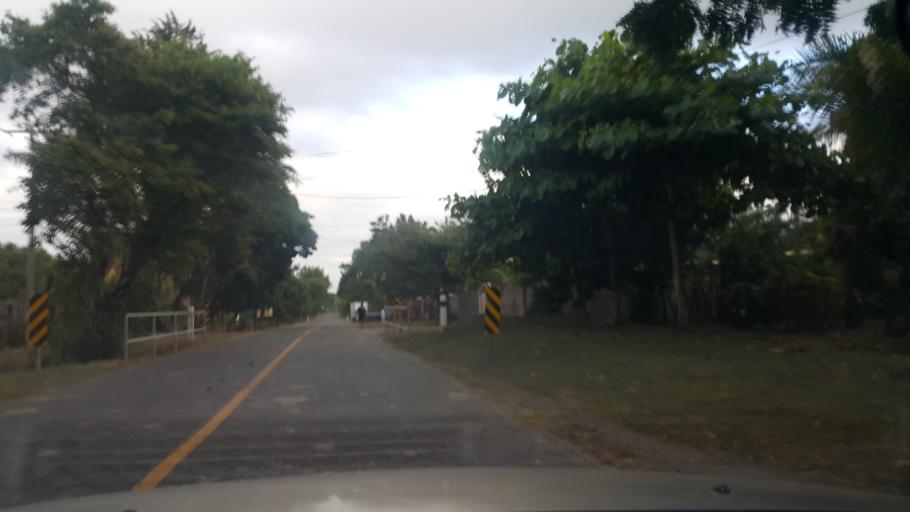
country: NI
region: Rivas
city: Moyogalpa
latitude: 11.5315
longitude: -85.6987
